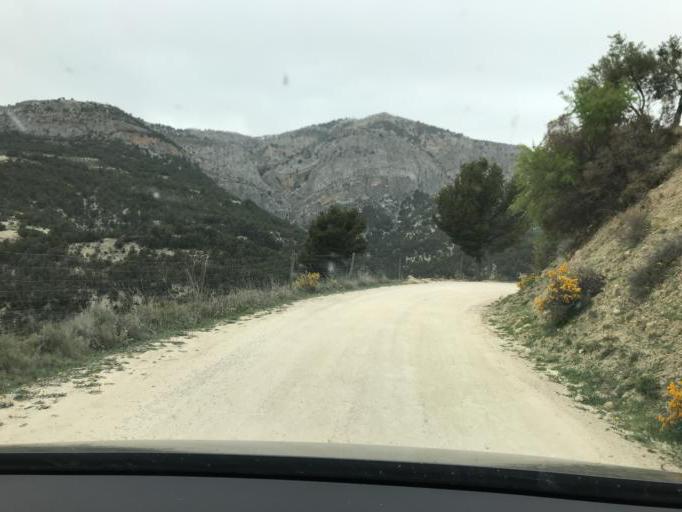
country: ES
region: Andalusia
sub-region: Provincia de Granada
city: Castril
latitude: 37.8296
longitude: -2.7729
